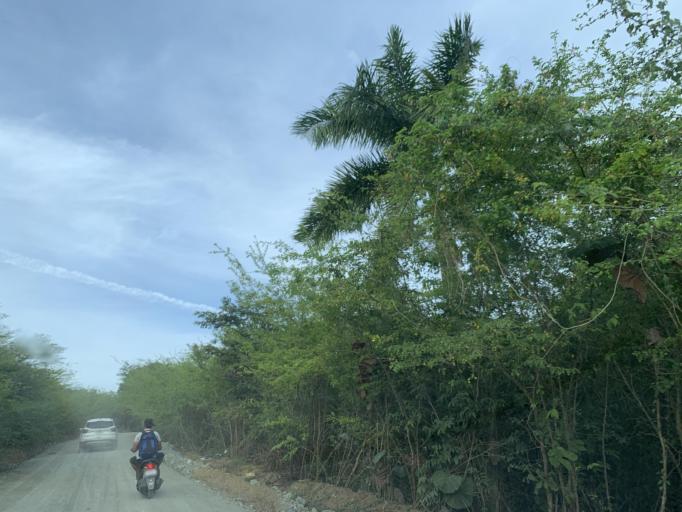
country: DO
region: Santiago
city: Pedro Garcia
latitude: 19.6981
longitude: -70.6150
